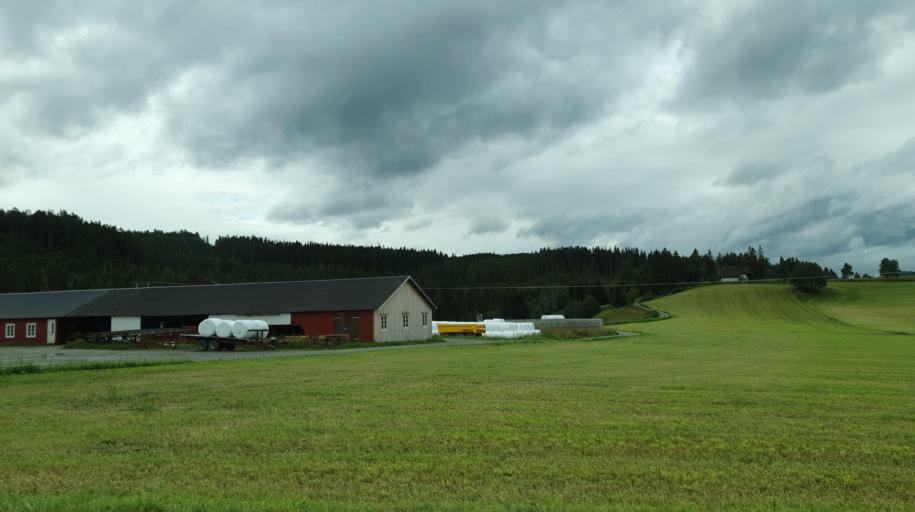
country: NO
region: Nord-Trondelag
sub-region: Stjordal
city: Stjordalshalsen
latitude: 63.4128
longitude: 10.9680
